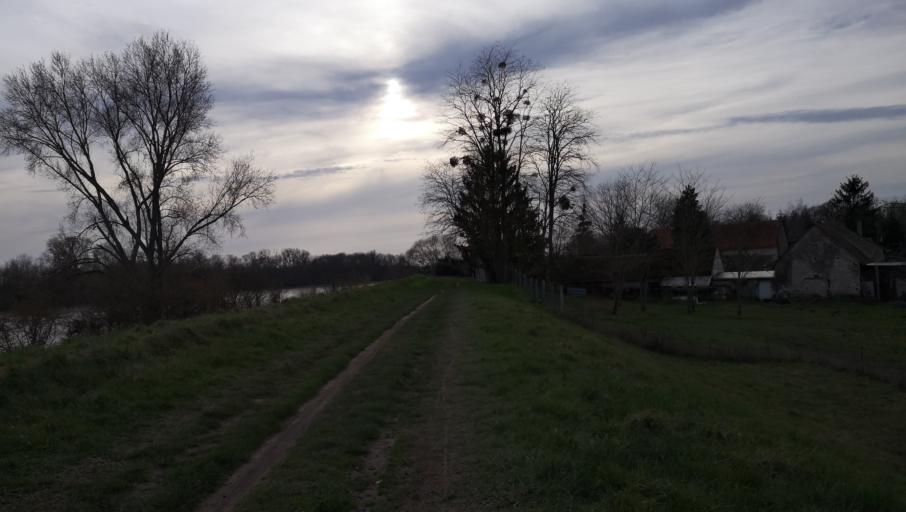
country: FR
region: Centre
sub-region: Departement du Loiret
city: Mareau-aux-Pres
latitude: 47.8675
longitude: 1.8054
